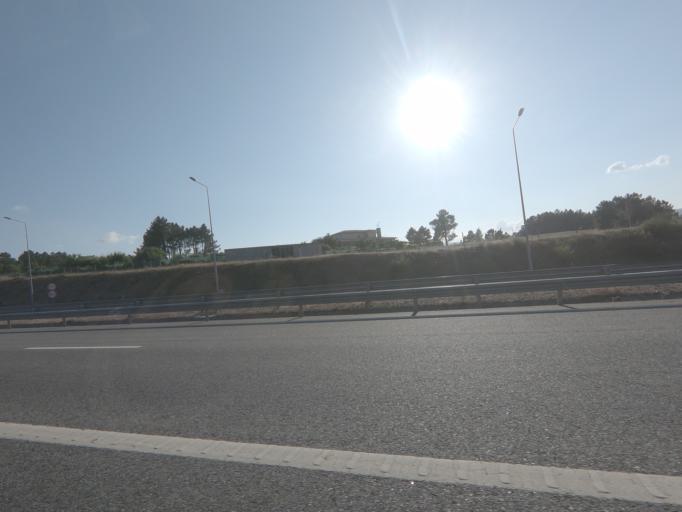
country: PT
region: Vila Real
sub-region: Chaves
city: Chaves
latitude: 41.8079
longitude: -7.4128
